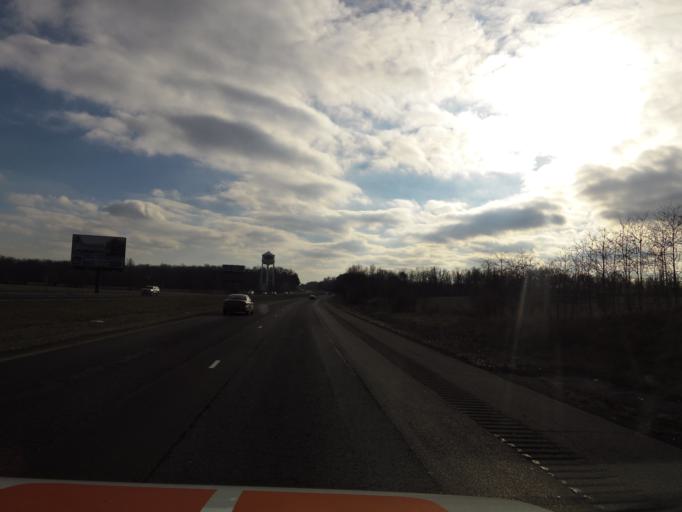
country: US
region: Indiana
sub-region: Scott County
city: Scottsburg
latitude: 38.6633
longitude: -85.7825
